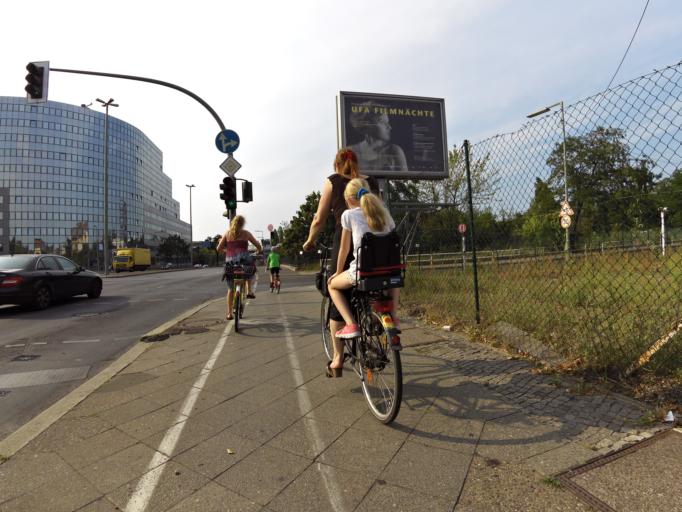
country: DE
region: Berlin
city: Berlin Schoeneberg
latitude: 52.4778
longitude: 13.3560
